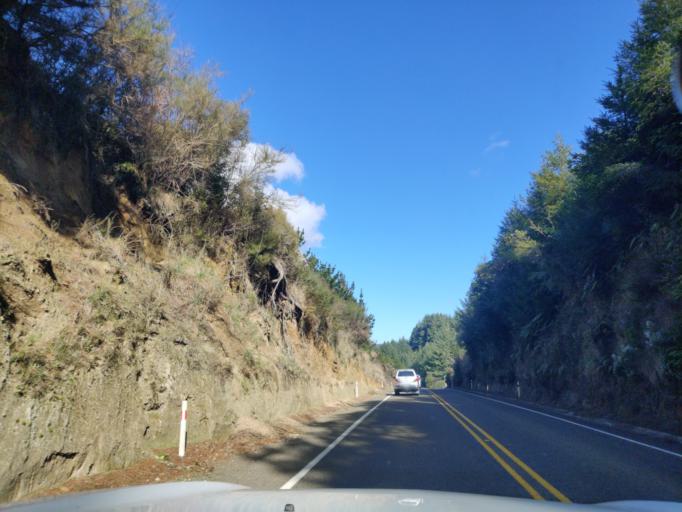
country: NZ
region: Waikato
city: Turangi
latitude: -38.6805
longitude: 175.6868
